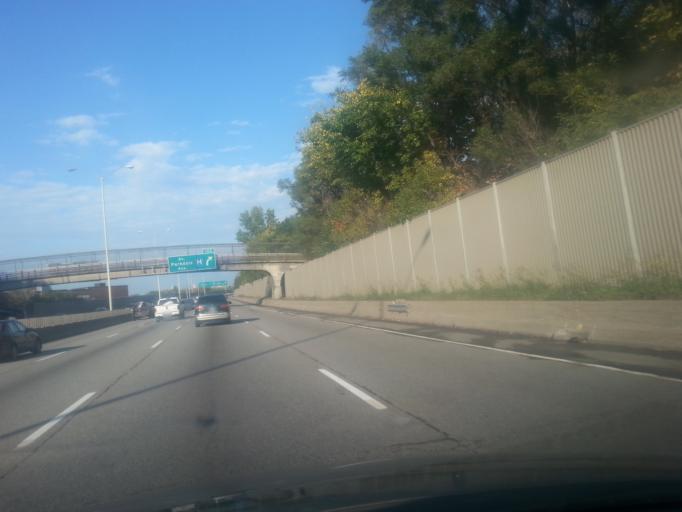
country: CA
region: Ontario
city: Ottawa
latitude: 45.3930
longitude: -75.7314
